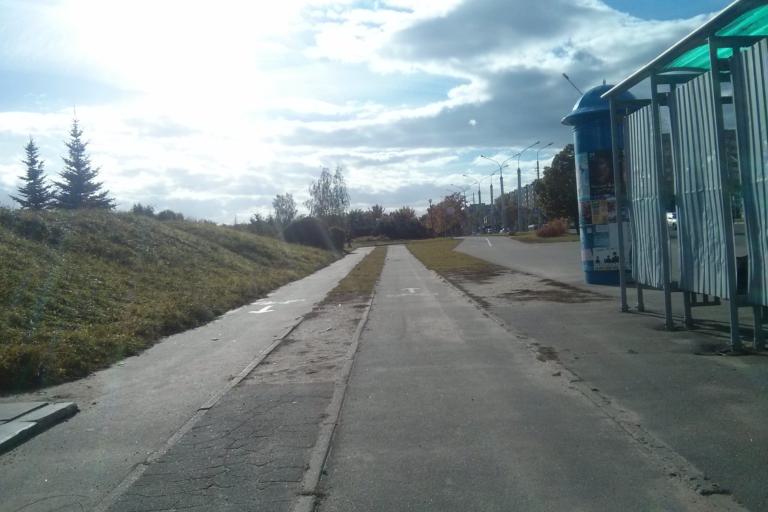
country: BY
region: Minsk
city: Minsk
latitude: 53.8525
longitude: 27.6160
